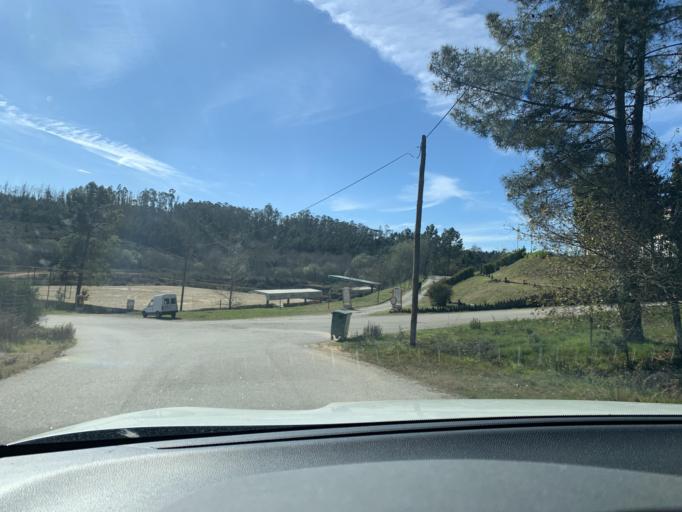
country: PT
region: Viseu
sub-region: Concelho de Tondela
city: Tondela
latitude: 40.6052
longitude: -8.0324
